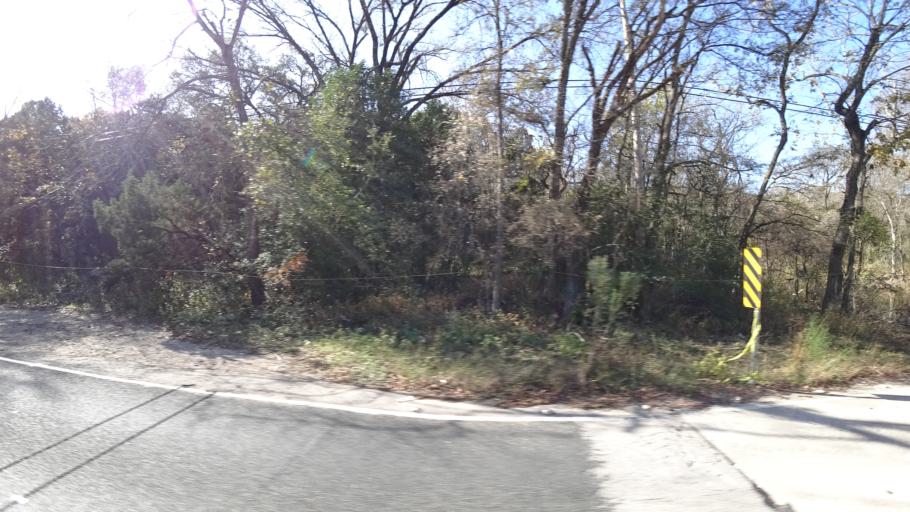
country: US
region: Texas
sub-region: Williamson County
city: Jollyville
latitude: 30.3902
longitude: -97.7746
